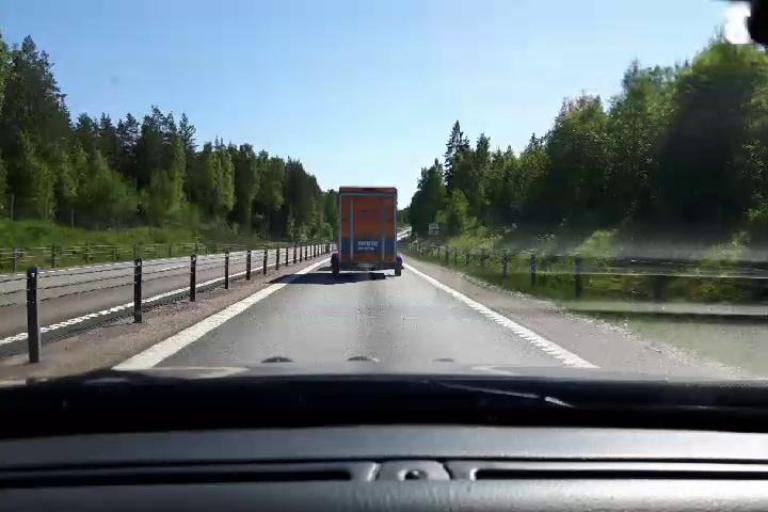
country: SE
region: Gaevleborg
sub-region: Soderhamns Kommun
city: Ljusne
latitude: 61.1423
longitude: 17.0302
